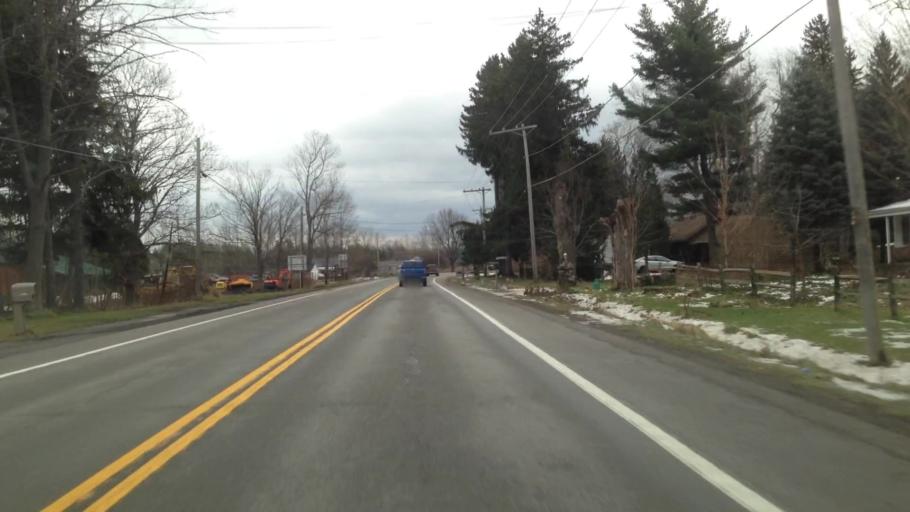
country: US
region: New York
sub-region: Erie County
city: Akron
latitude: 42.9980
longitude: -78.4651
